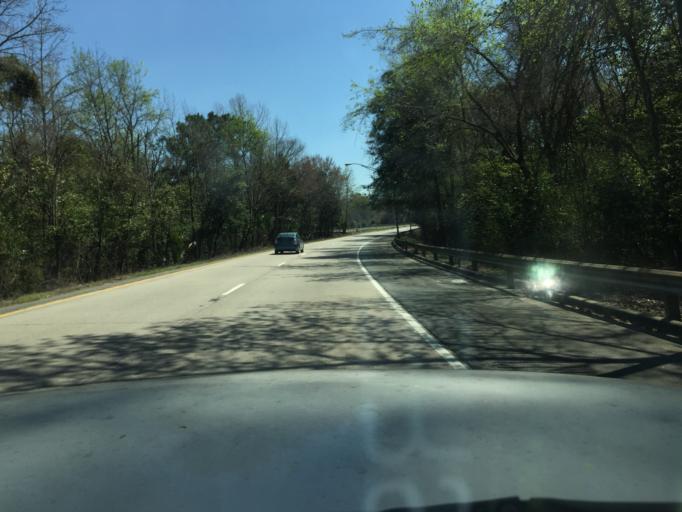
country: US
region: Georgia
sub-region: Chatham County
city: Savannah
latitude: 32.0655
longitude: -81.1132
